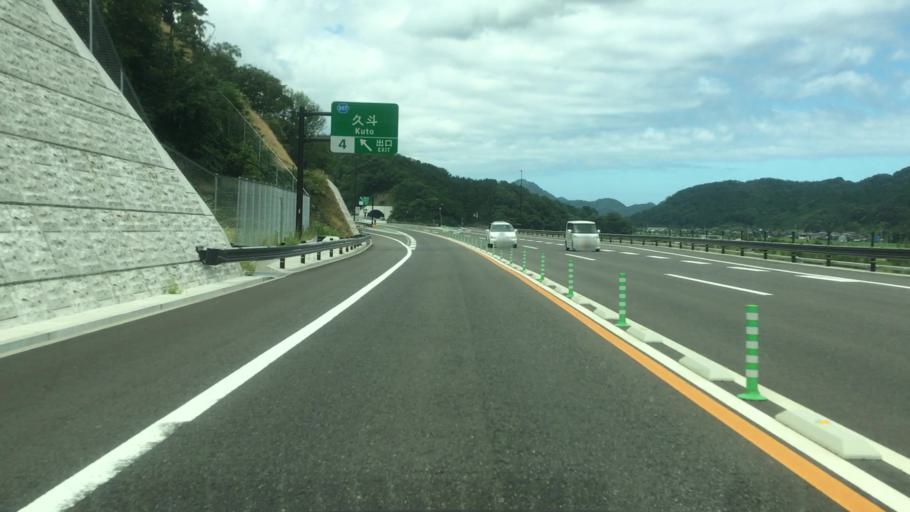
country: JP
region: Tottori
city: Tottori
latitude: 35.6221
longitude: 134.5042
